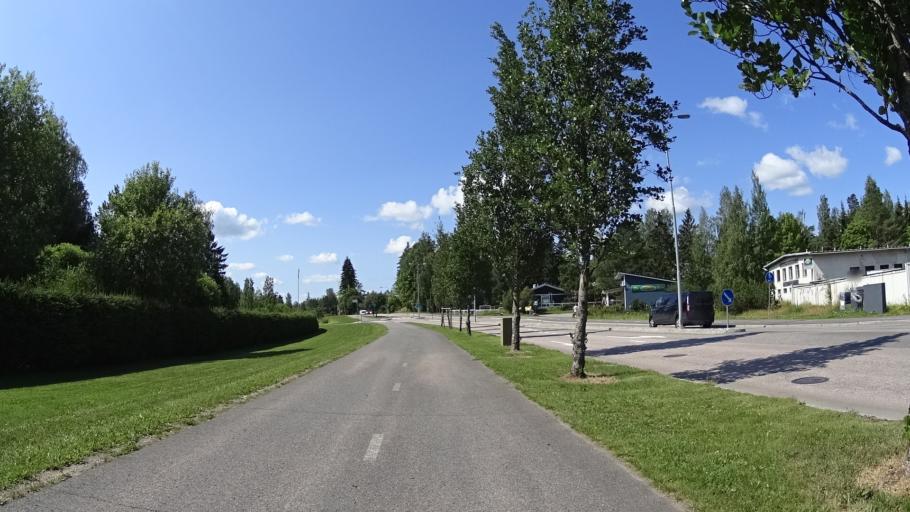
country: FI
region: Uusimaa
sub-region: Helsinki
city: Jaervenpaeae
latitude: 60.4708
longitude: 25.0763
